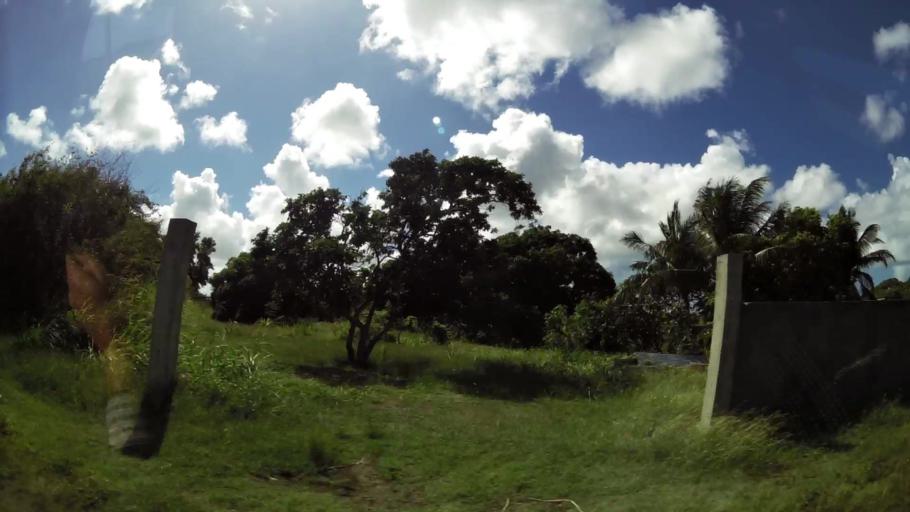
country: GP
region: Guadeloupe
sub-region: Guadeloupe
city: Anse-Bertrand
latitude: 16.4661
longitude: -61.4925
